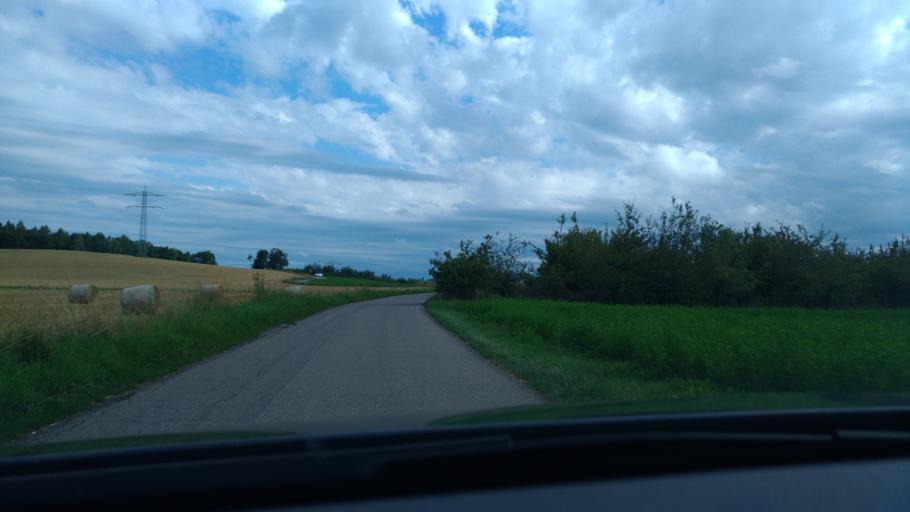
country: DE
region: Baden-Wuerttemberg
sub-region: Tuebingen Region
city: Sipplingen
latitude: 47.8010
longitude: 9.1228
